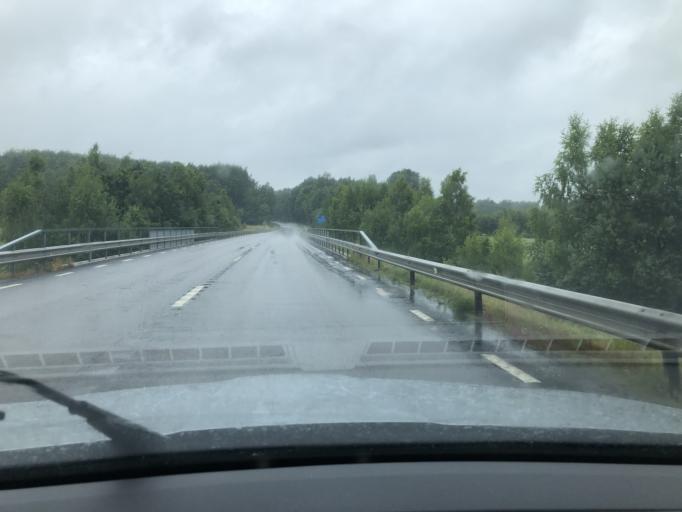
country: SE
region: Blekinge
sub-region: Olofstroms Kommun
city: Jamshog
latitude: 56.2417
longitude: 14.5389
